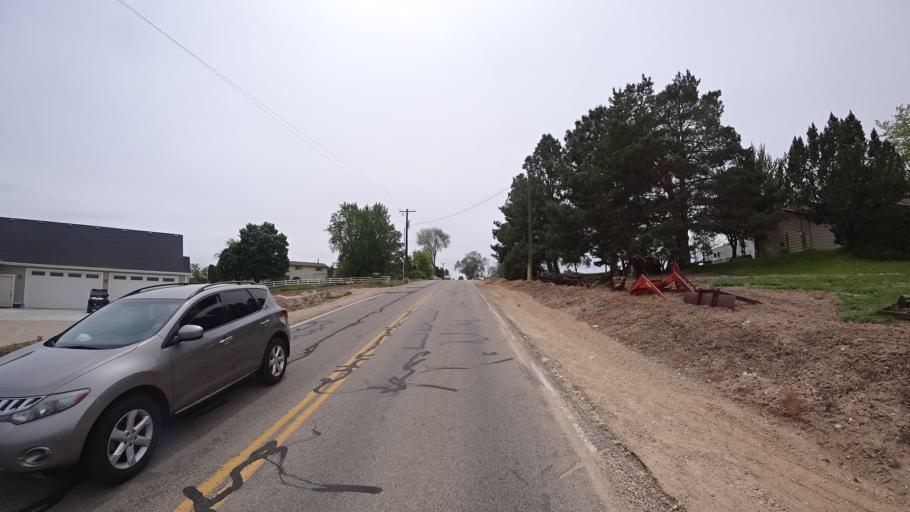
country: US
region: Idaho
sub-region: Ada County
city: Meridian
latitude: 43.5589
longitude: -116.3746
